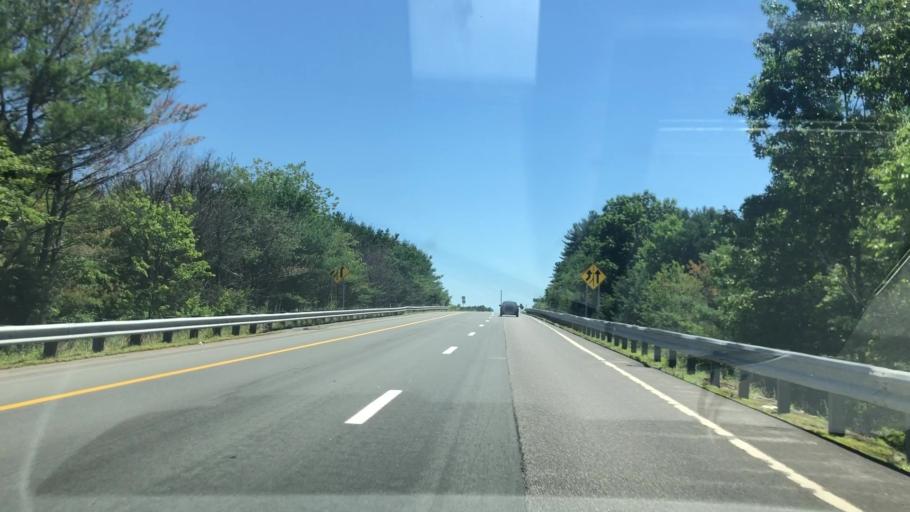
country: US
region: New Hampshire
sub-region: Hillsborough County
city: Manchester
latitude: 42.9588
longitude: -71.4102
